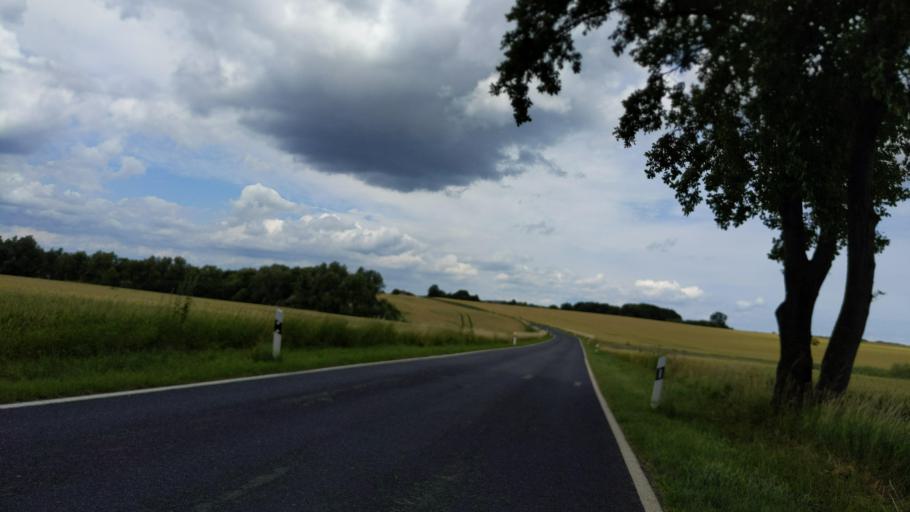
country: DE
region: Mecklenburg-Vorpommern
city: Dassow
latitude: 53.9460
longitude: 10.9731
